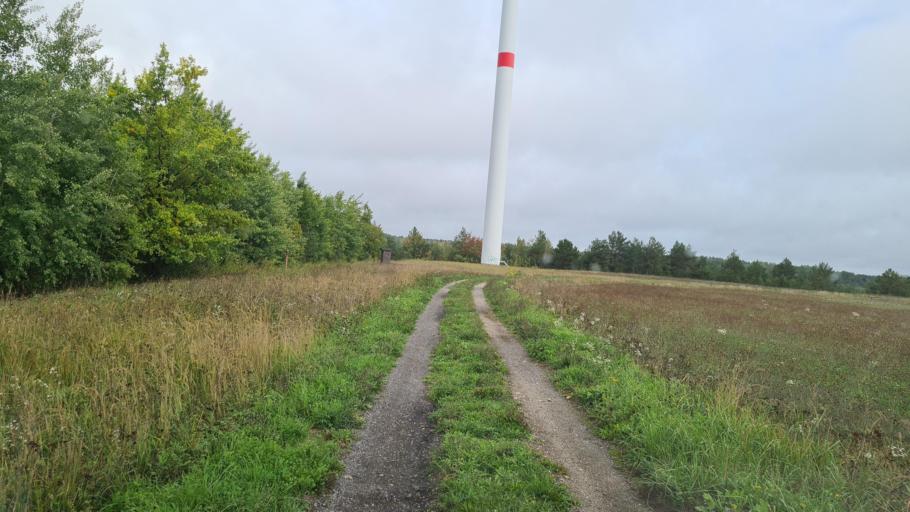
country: DE
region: Brandenburg
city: Sallgast
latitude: 51.5606
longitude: 13.8232
